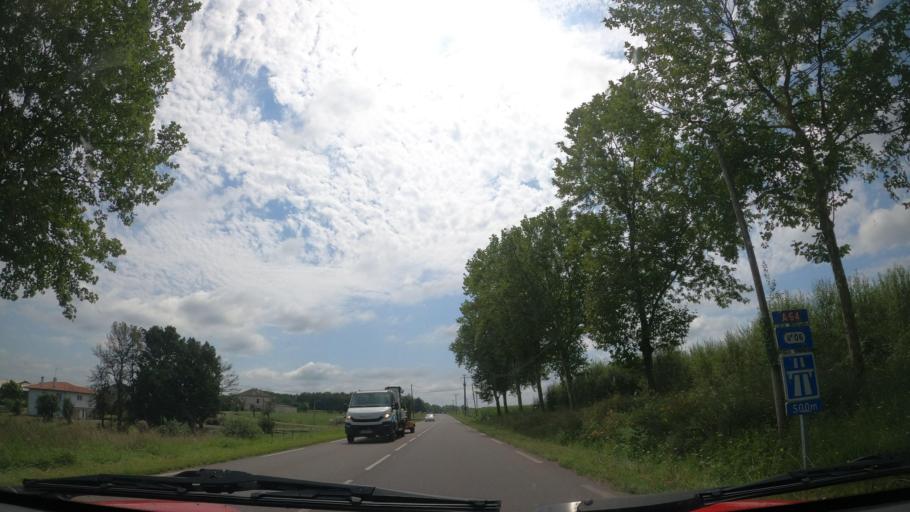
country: FR
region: Aquitaine
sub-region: Departement des Landes
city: Peyrehorade
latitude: 43.5231
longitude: -1.1048
